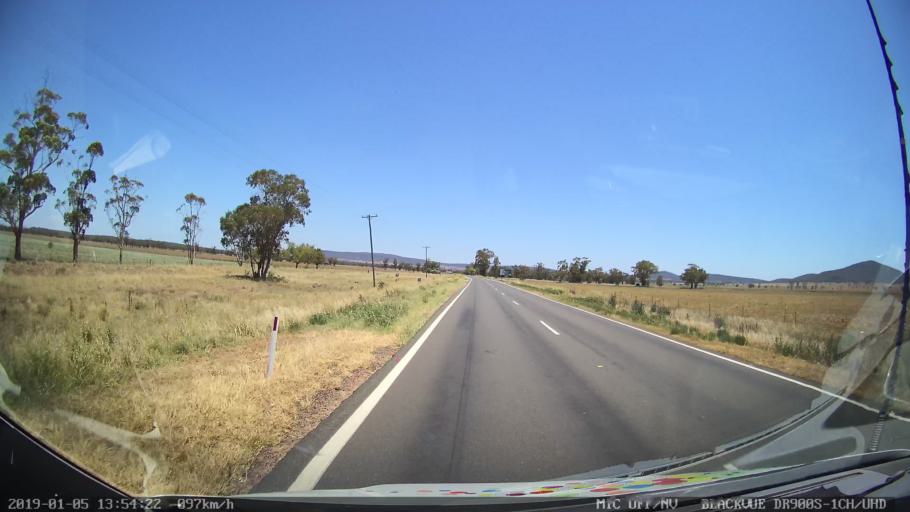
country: AU
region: New South Wales
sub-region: Gunnedah
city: Gunnedah
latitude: -31.0878
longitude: 150.2742
